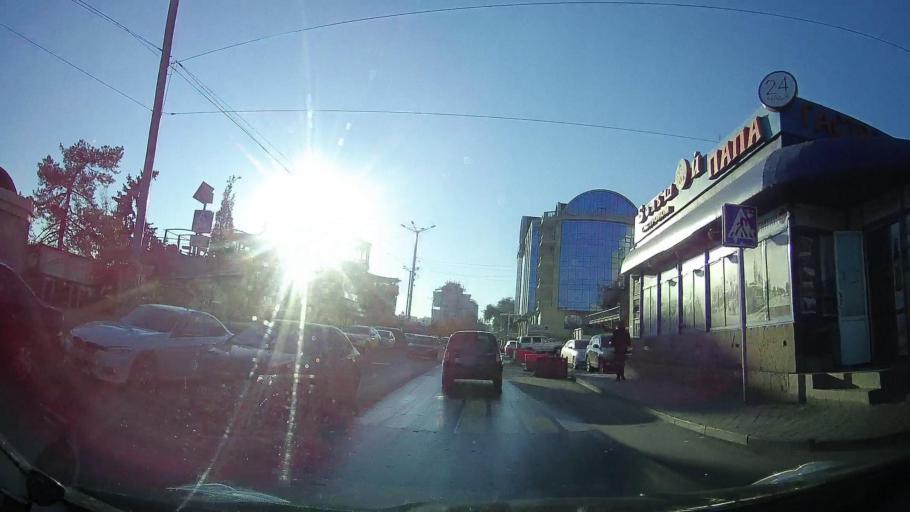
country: RU
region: Rostov
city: Rostov-na-Donu
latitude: 47.2142
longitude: 39.7158
